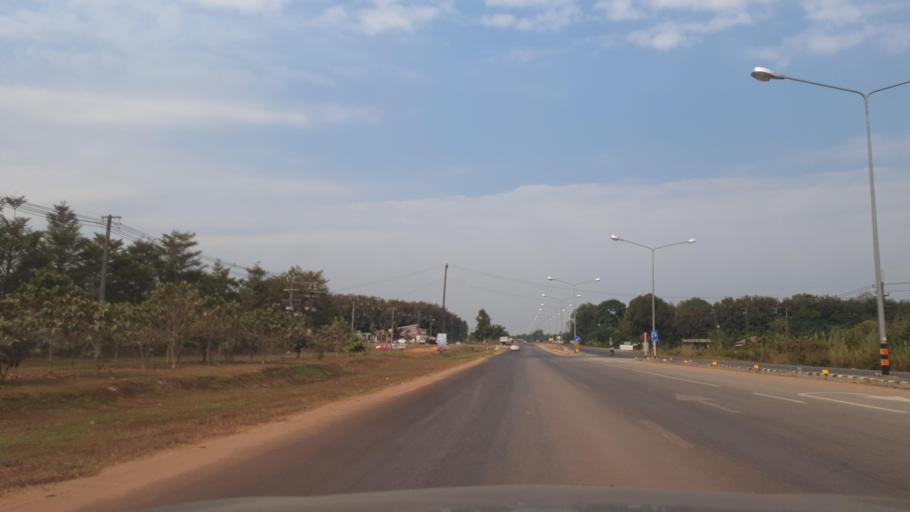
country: TH
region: Changwat Bueng Kan
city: Si Wilai
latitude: 18.2977
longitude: 103.8180
